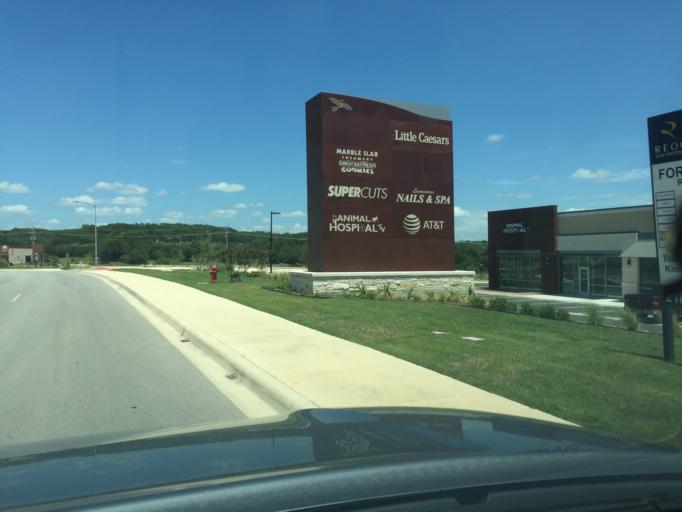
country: US
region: Texas
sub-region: Comal County
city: Bulverde
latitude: 29.7997
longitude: -98.4214
